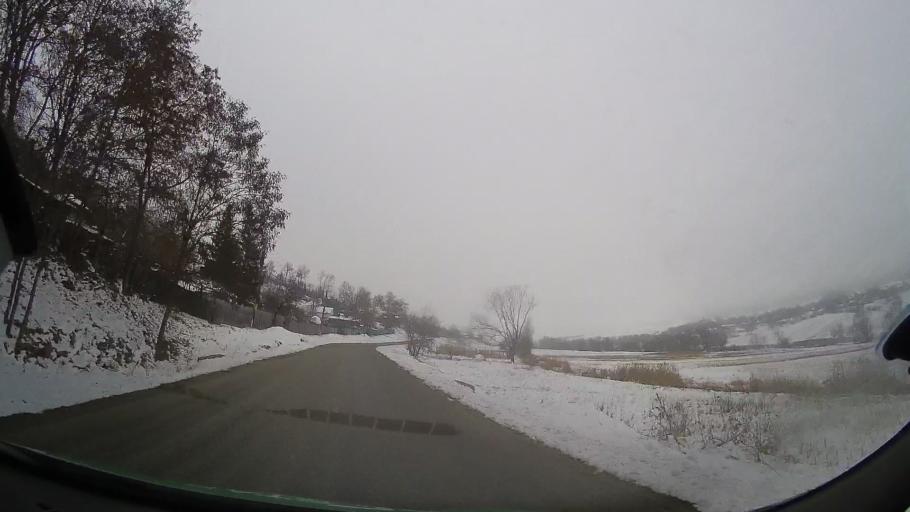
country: RO
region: Bacau
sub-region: Comuna Vultureni
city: Vultureni
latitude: 46.3336
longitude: 27.2916
